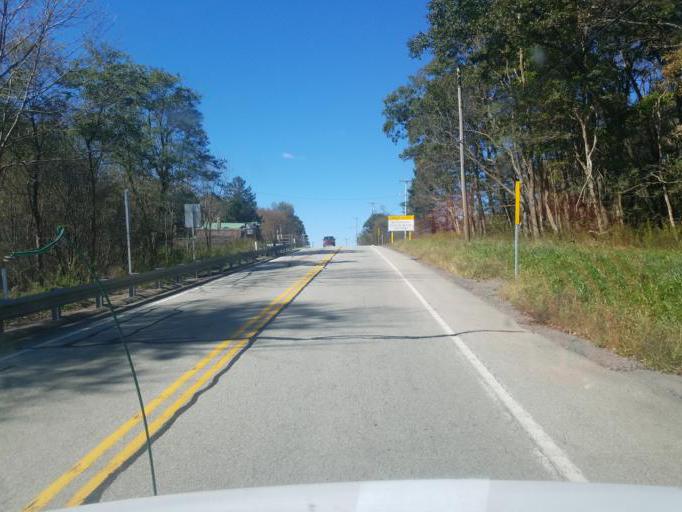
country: US
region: Pennsylvania
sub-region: Westmoreland County
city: Waterford
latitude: 40.1792
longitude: -79.1303
